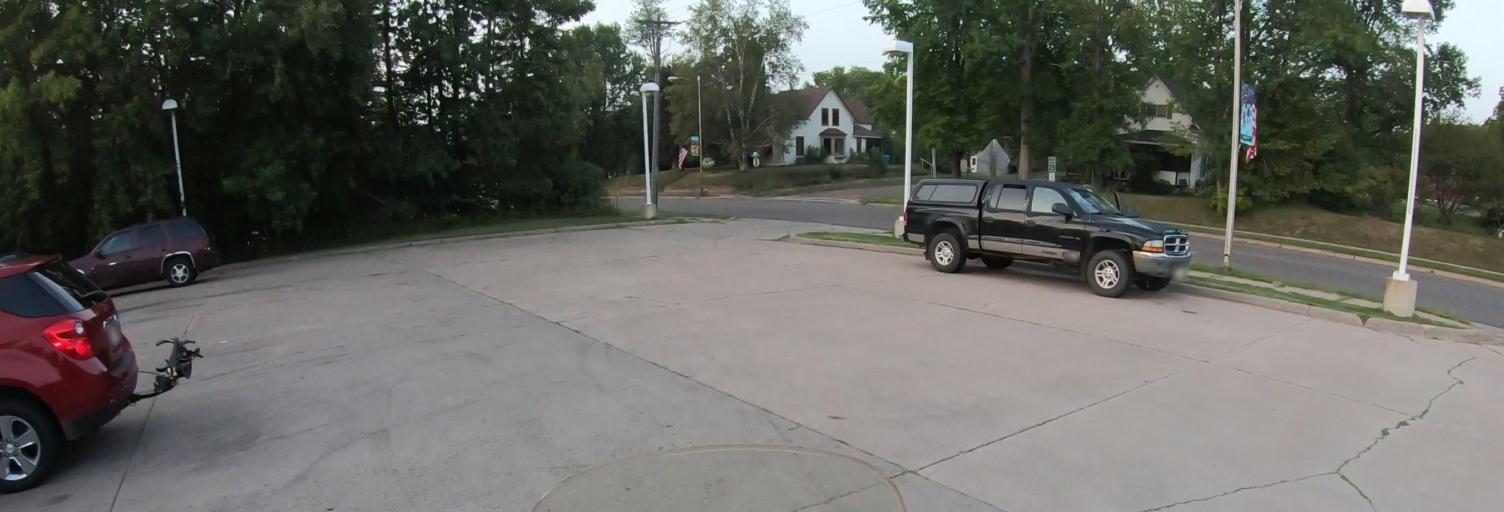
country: US
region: Wisconsin
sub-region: Burnett County
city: Grantsburg
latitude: 45.7736
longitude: -92.6824
